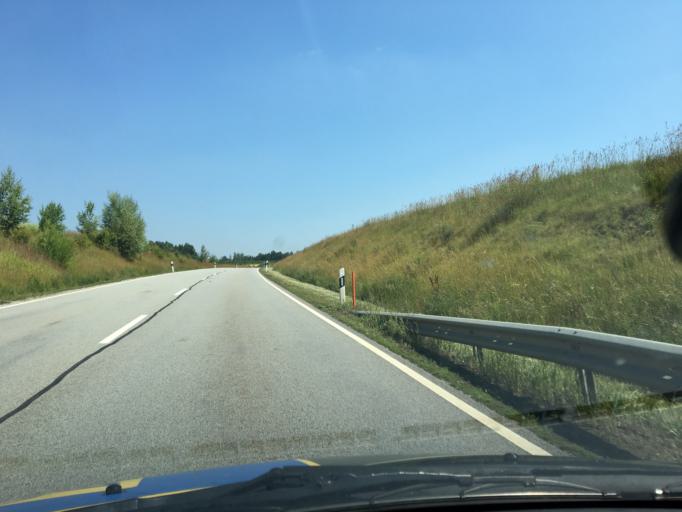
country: DE
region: Bavaria
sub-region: Upper Bavaria
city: Neumarkt-Sankt Veit
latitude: 48.3551
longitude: 12.4894
